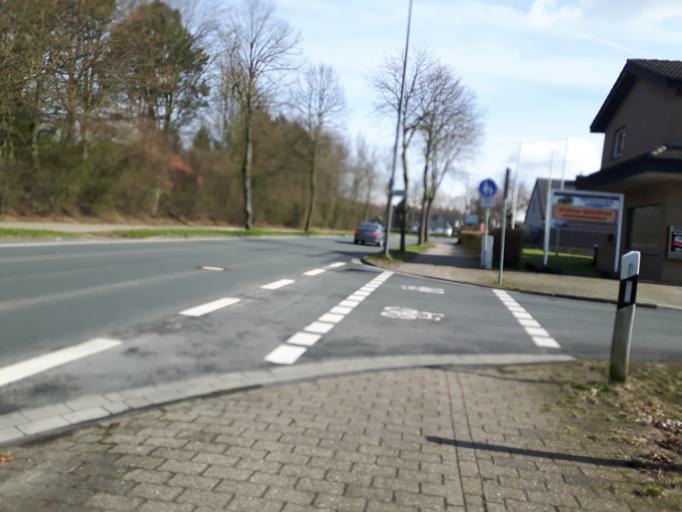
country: DE
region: North Rhine-Westphalia
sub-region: Regierungsbezirk Munster
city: Dulmen
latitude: 51.8334
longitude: 7.3042
